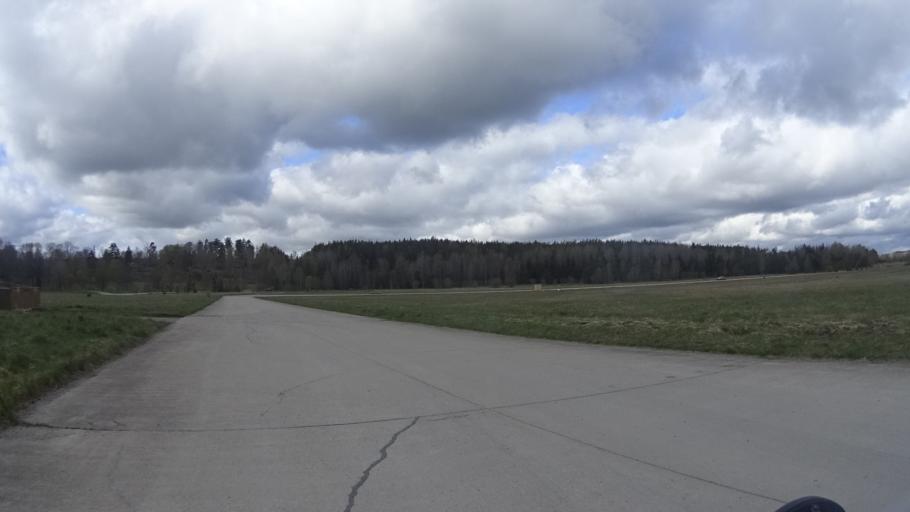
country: SE
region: Stockholm
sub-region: Botkyrka Kommun
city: Tullinge
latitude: 59.1728
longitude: 17.9239
